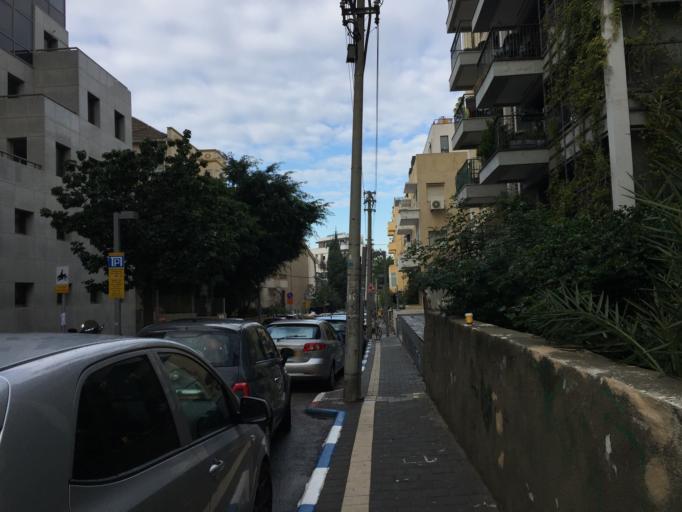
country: IL
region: Tel Aviv
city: Tel Aviv
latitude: 32.0661
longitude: 34.7740
